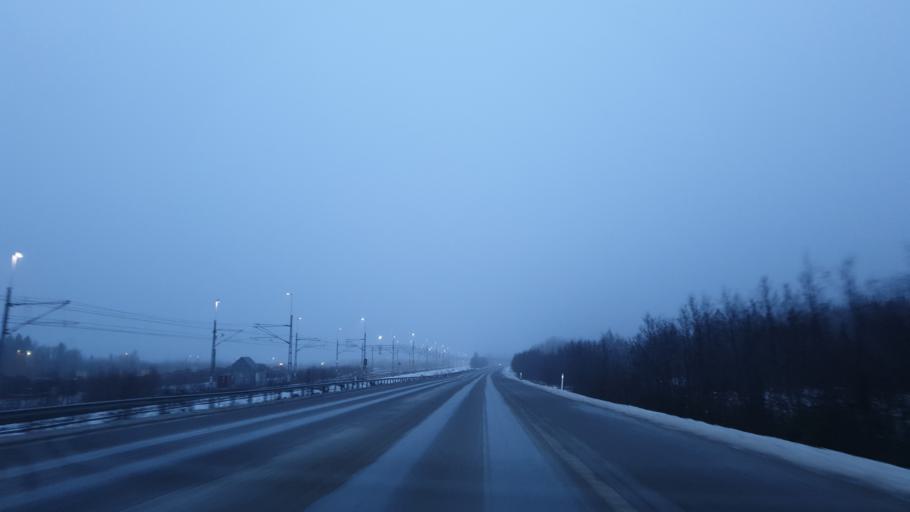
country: SE
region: Vaesterbotten
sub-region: Umea Kommun
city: Umea
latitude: 63.7824
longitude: 20.3213
